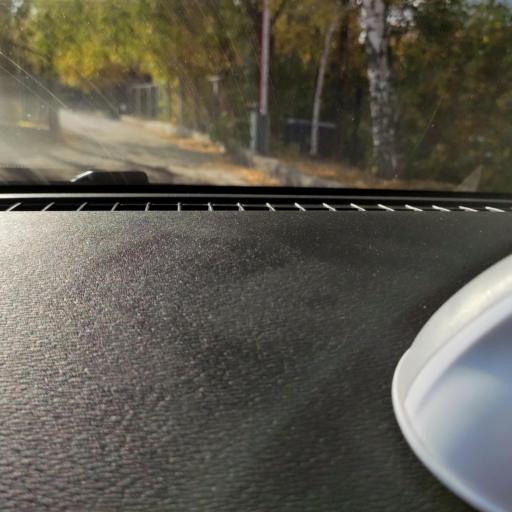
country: RU
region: Samara
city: Samara
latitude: 53.2363
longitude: 50.1855
